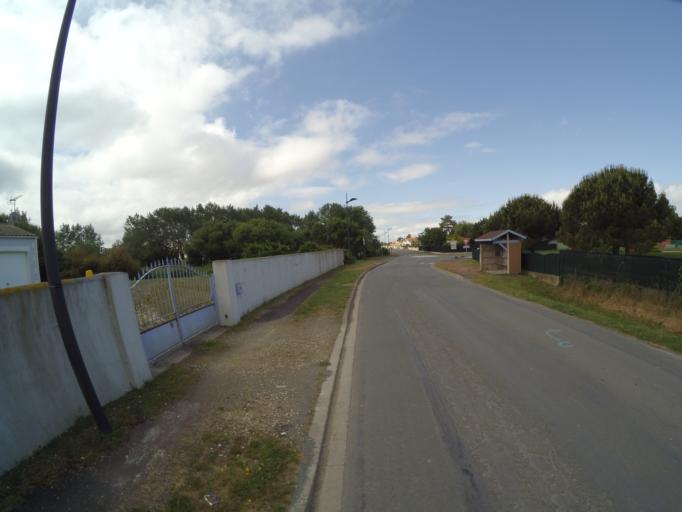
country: FR
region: Poitou-Charentes
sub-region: Departement de la Charente-Maritime
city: Chatelaillon-Plage
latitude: 46.0570
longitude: -1.0759
